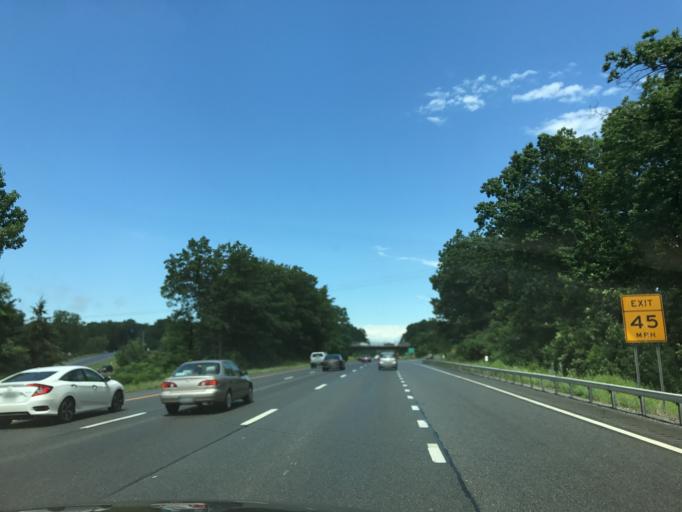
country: US
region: New York
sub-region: Saratoga County
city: Country Knolls
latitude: 42.9001
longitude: -73.7837
